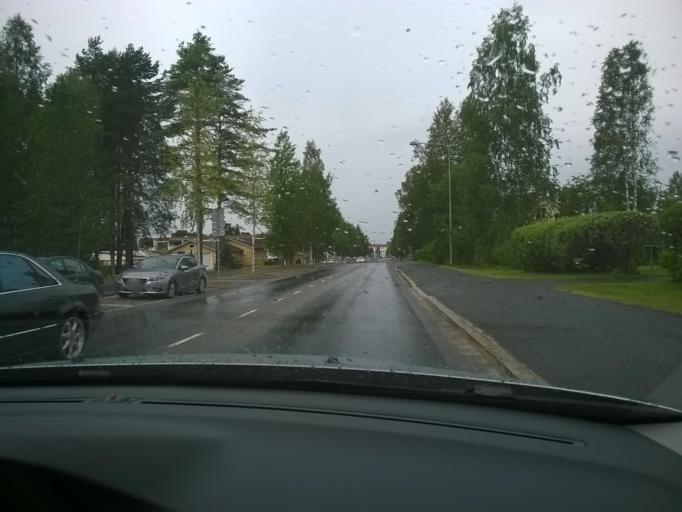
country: FI
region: Kainuu
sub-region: Kehys-Kainuu
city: Kuhmo
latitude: 64.1252
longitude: 29.5296
